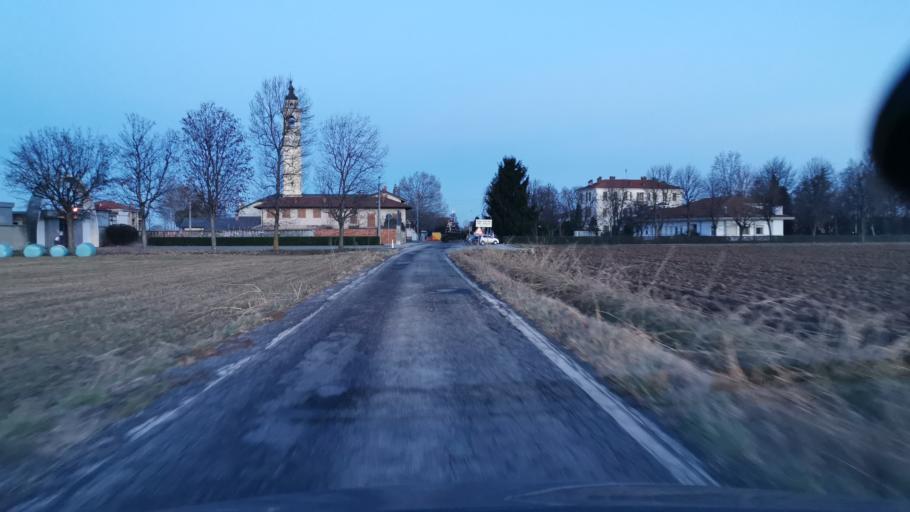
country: IT
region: Piedmont
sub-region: Provincia di Cuneo
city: Roata Rossi
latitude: 44.4532
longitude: 7.4882
